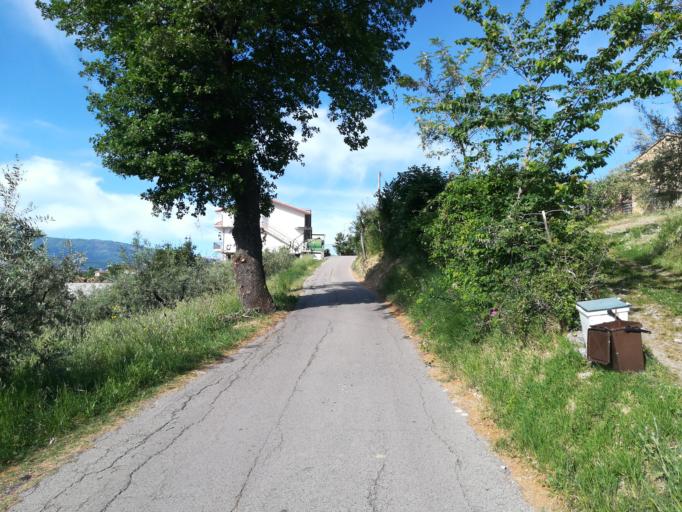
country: IT
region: Abruzzo
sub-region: Provincia di Chieti
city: Bucchianico
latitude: 42.2962
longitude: 14.1713
